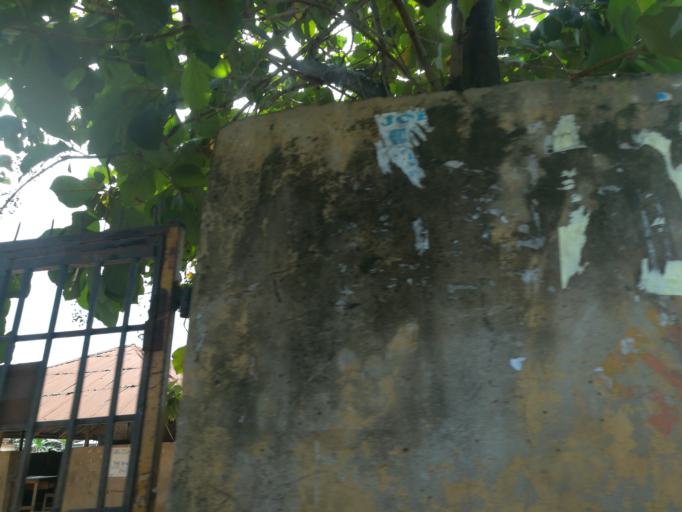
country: NG
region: Lagos
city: Agege
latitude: 6.6072
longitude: 3.3272
